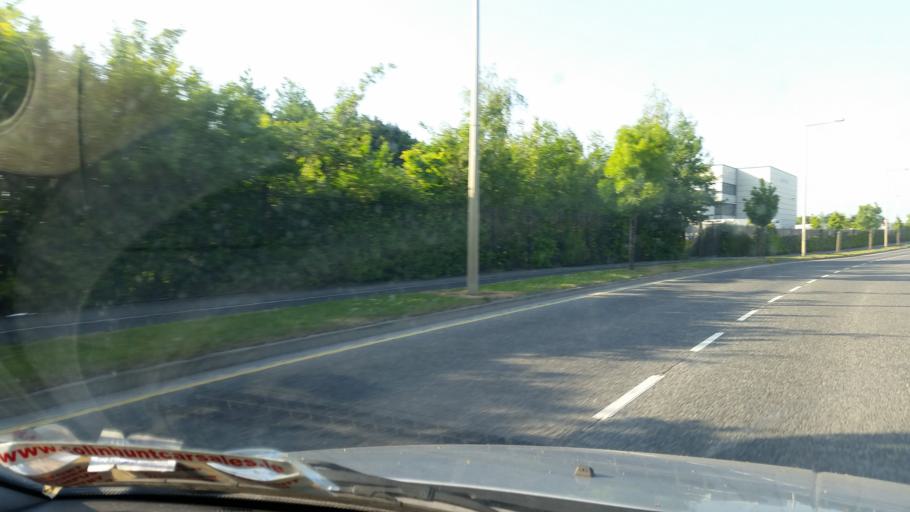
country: IE
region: Leinster
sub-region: Fingal County
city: Blanchardstown
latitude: 53.4110
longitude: -6.3680
